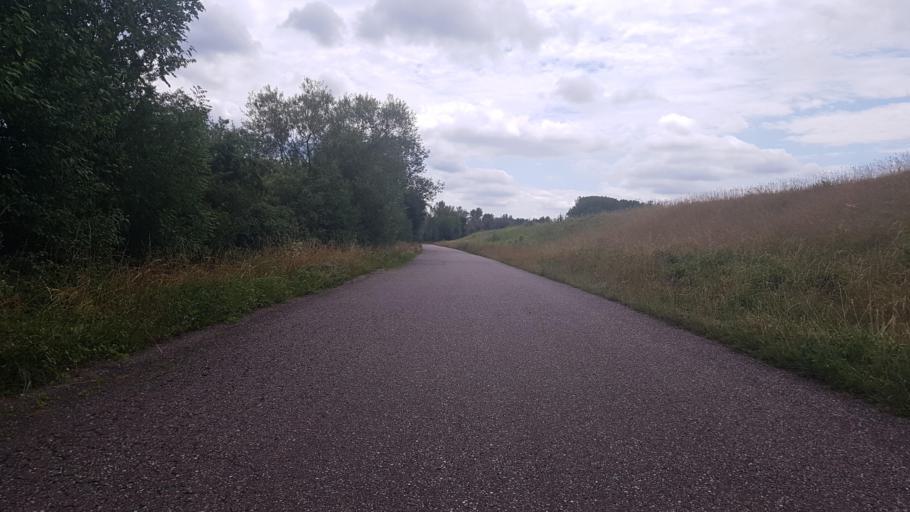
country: DE
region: Baden-Wuerttemberg
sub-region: Karlsruhe Region
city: Hugelsheim
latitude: 48.8295
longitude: 8.1008
